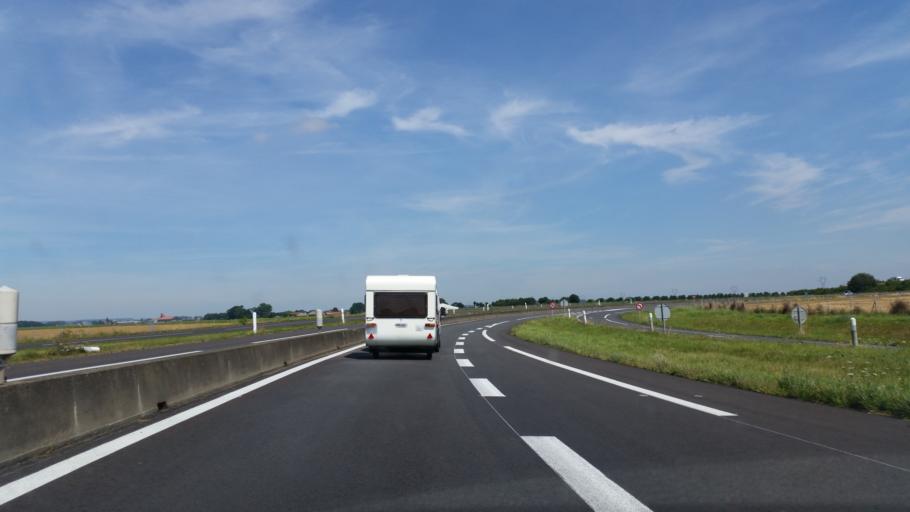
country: FR
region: Picardie
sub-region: Departement de la Somme
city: Chaulnes
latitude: 49.8511
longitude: 2.8142
